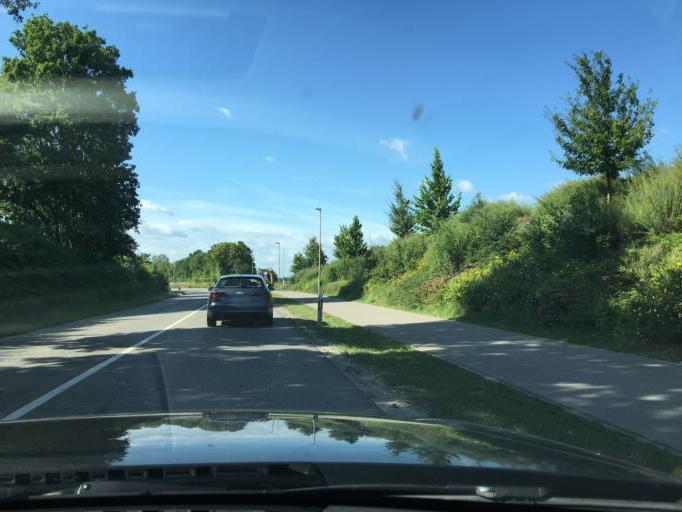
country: DE
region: Bavaria
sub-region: Upper Bavaria
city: Gaimersheim
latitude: 48.7985
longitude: 11.3652
